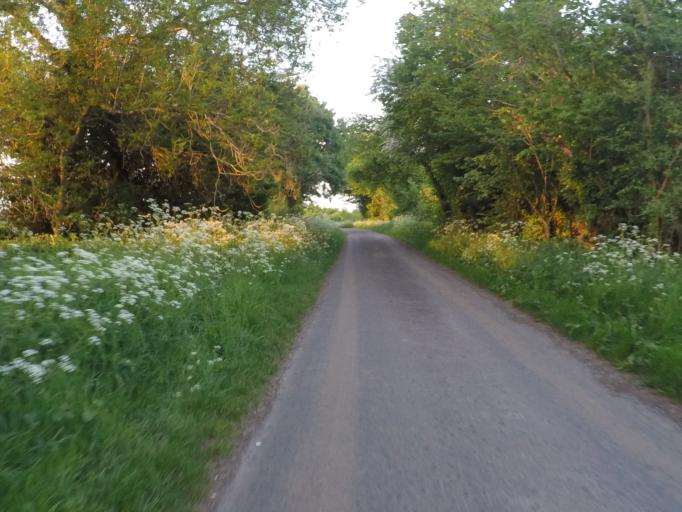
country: GB
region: England
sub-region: Oxfordshire
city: North Leigh
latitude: 51.8250
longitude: -1.4808
